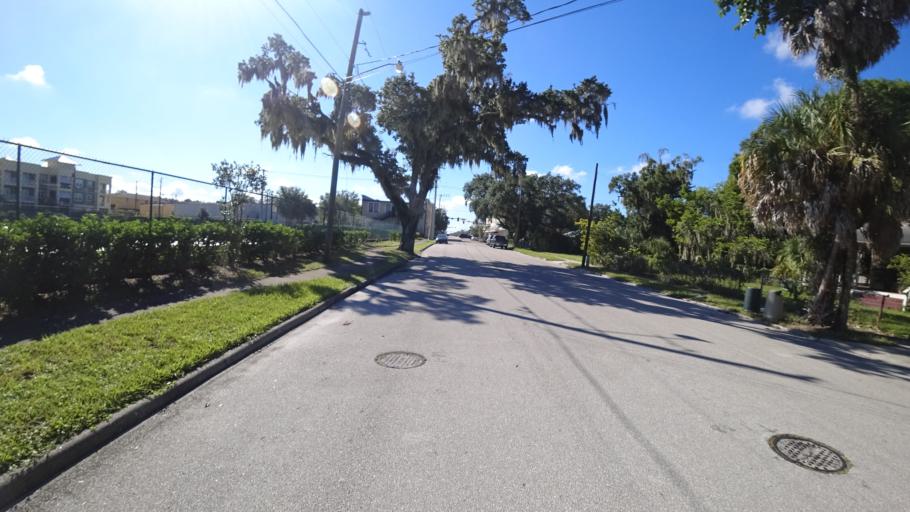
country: US
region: Florida
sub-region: Manatee County
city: Bradenton
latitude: 27.4963
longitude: -82.5547
